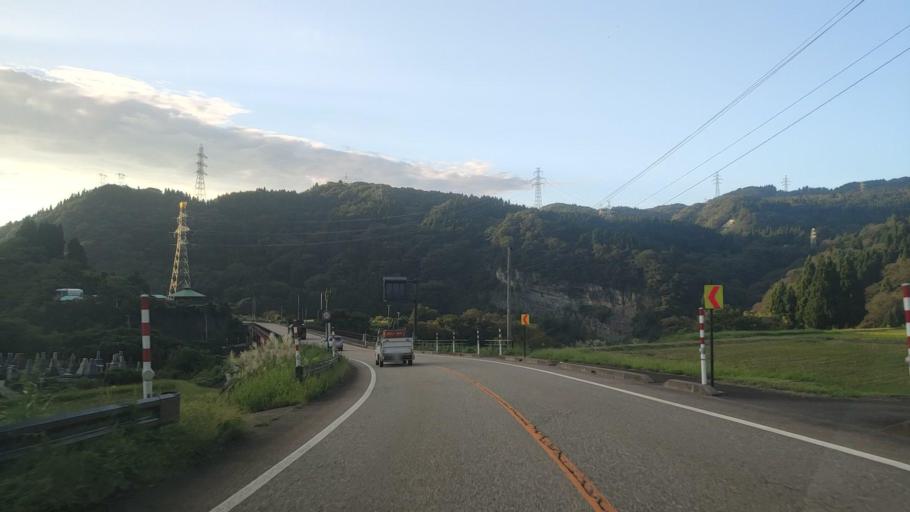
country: JP
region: Toyama
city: Nanto-shi
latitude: 36.5620
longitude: 137.0071
